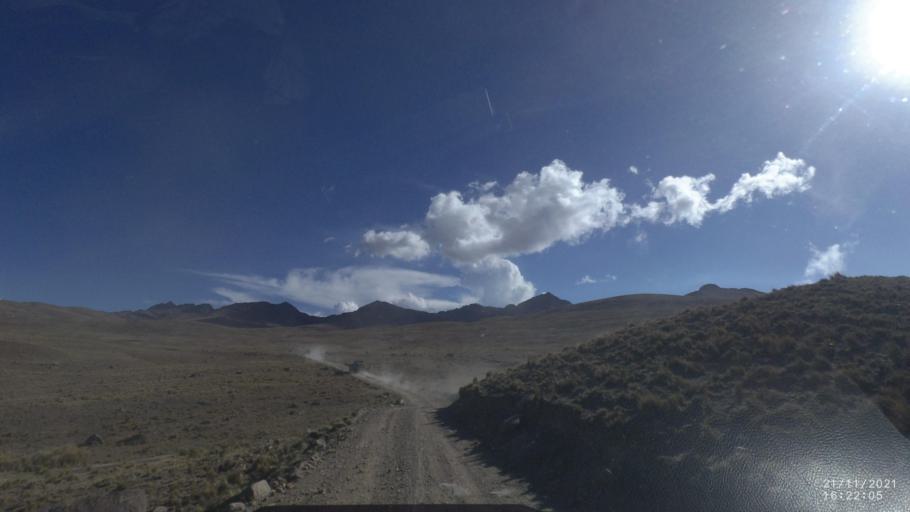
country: BO
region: Cochabamba
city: Cochabamba
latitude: -17.0174
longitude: -66.2856
